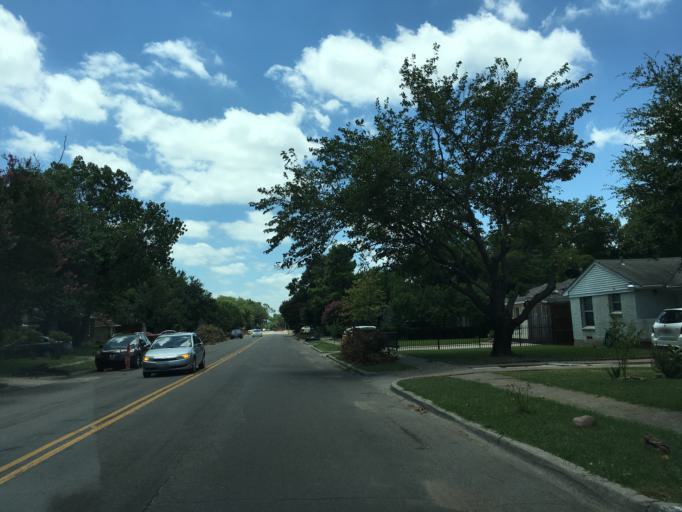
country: US
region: Texas
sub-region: Dallas County
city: Garland
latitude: 32.8452
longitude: -96.6730
